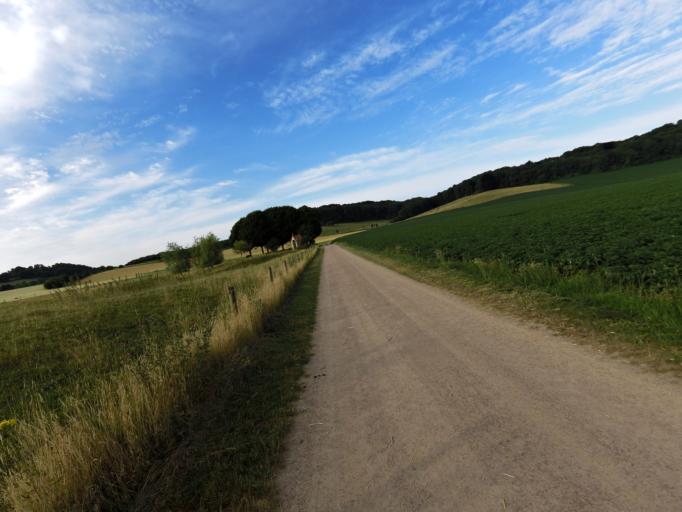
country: NL
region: Limburg
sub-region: Valkenburg aan de Geul
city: Schin op Geul
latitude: 50.8544
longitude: 5.8516
